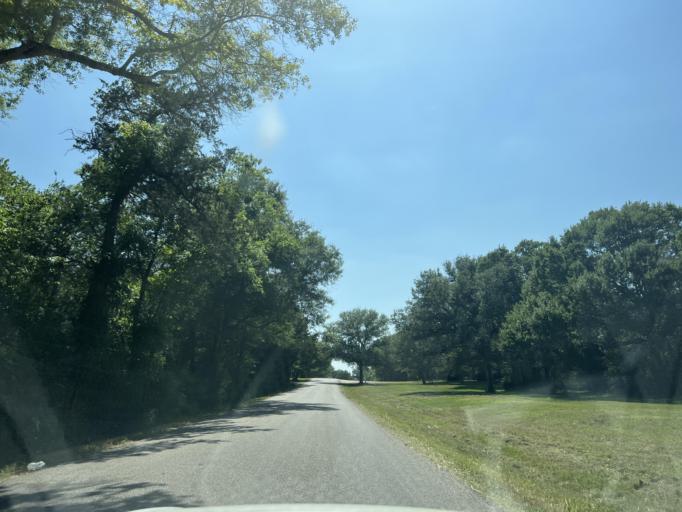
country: US
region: Texas
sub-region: Washington County
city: Brenham
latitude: 30.1612
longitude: -96.4291
